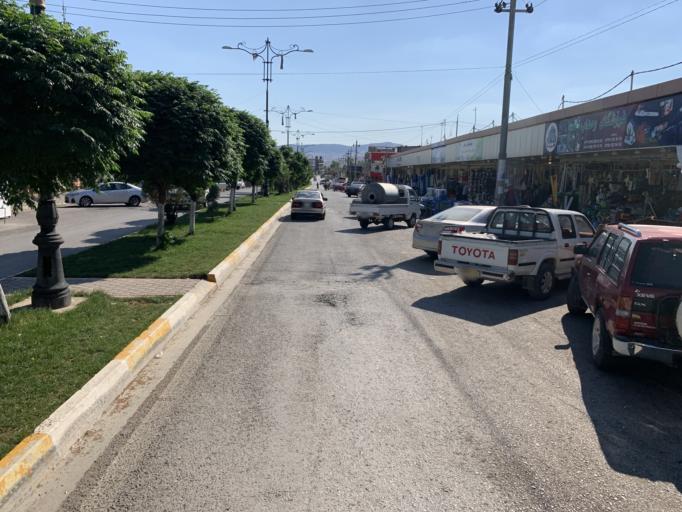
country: IQ
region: As Sulaymaniyah
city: Raniye
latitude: 36.2344
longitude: 44.7916
